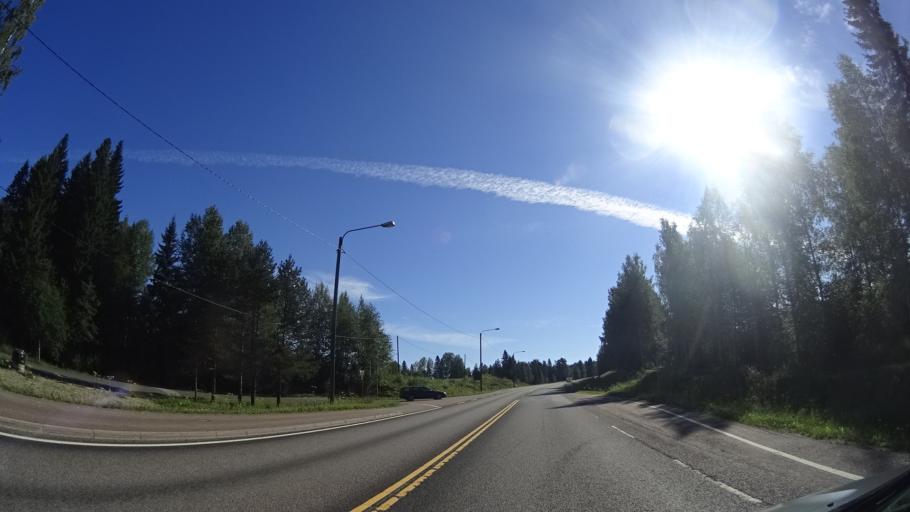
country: FI
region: Central Finland
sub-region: Jyvaeskylae
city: Petaejaevesi
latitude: 62.2710
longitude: 25.3107
